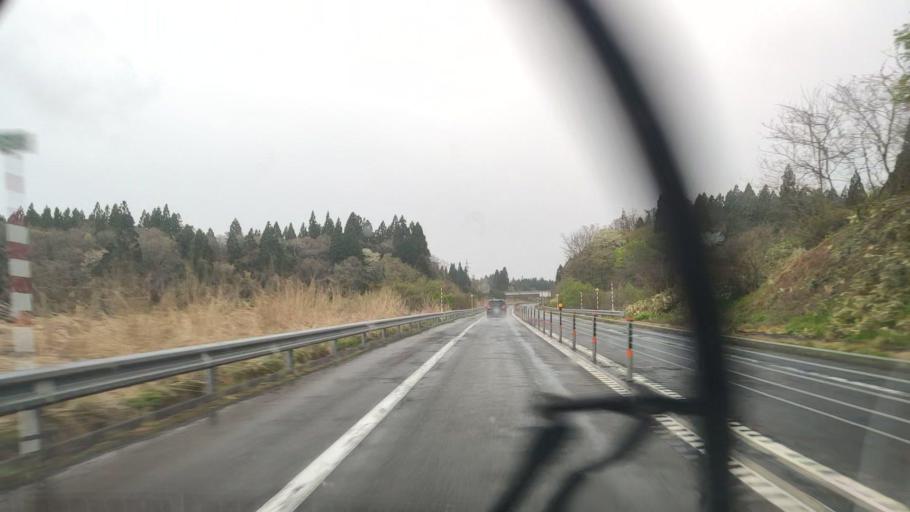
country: JP
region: Akita
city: Noshiromachi
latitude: 40.1708
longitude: 140.0528
